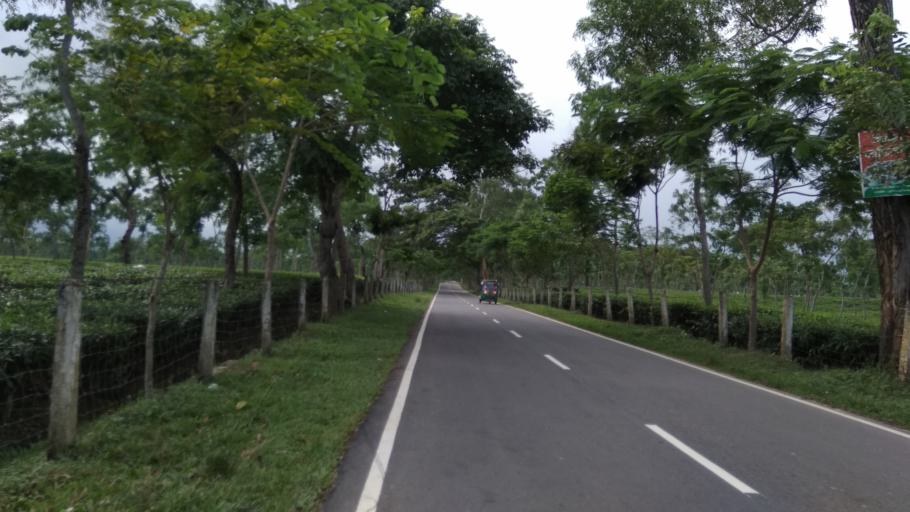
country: IN
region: Tripura
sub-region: Dhalai
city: Kamalpur
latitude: 24.3021
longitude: 91.7452
